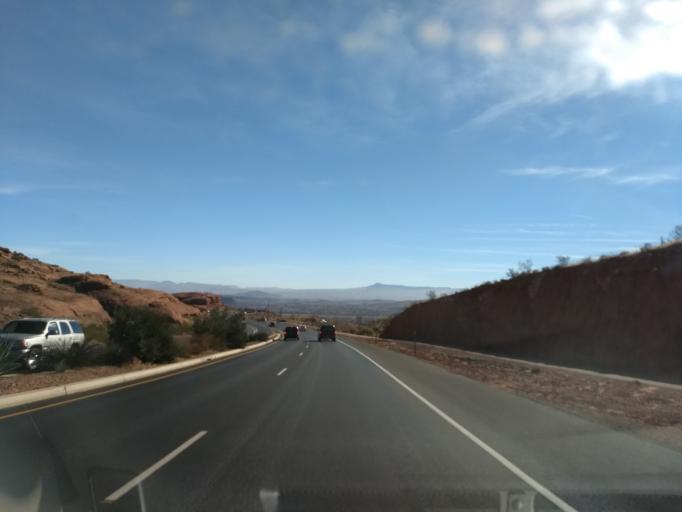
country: US
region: Utah
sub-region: Washington County
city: Saint George
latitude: 37.1199
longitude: -113.5833
